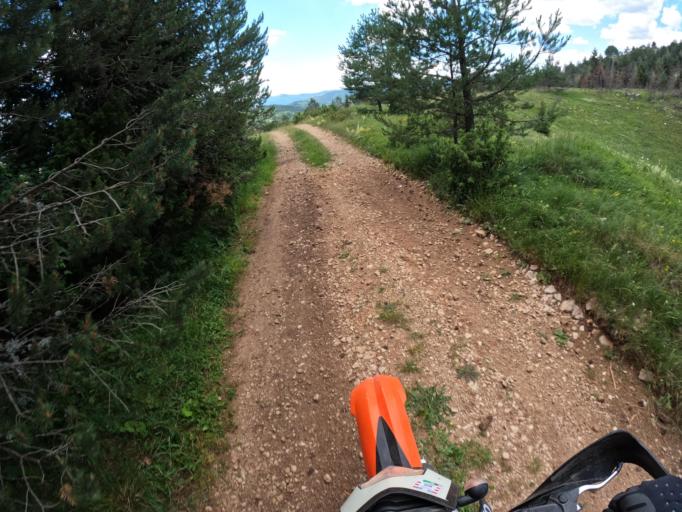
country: BA
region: Federation of Bosnia and Herzegovina
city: Livno
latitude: 43.9683
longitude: 17.1527
